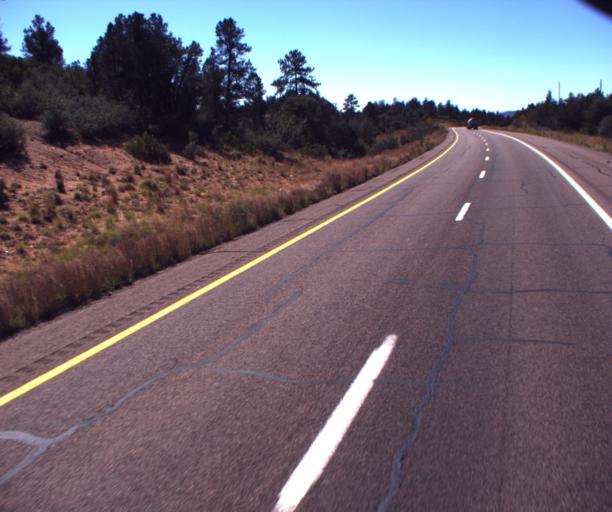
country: US
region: Arizona
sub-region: Gila County
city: Star Valley
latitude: 34.2765
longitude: -111.1737
